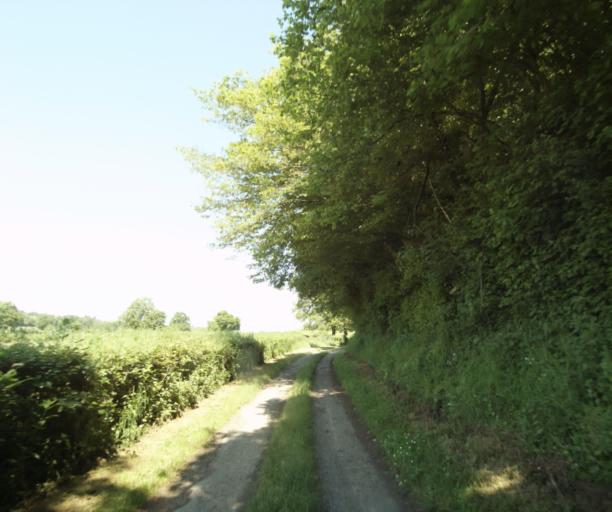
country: FR
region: Bourgogne
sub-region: Departement de Saone-et-Loire
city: Palinges
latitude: 46.5775
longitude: 4.1737
